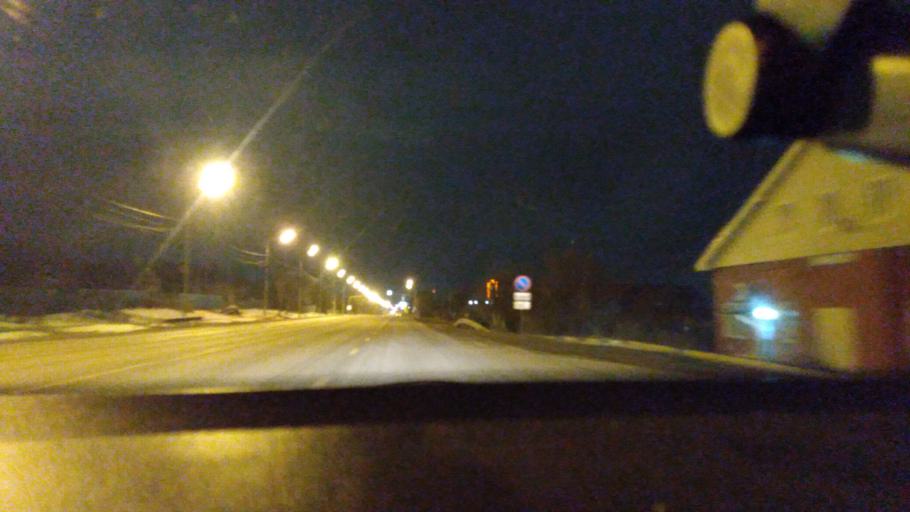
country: RU
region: Moskovskaya
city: Bronnitsy
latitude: 55.4078
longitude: 38.2975
